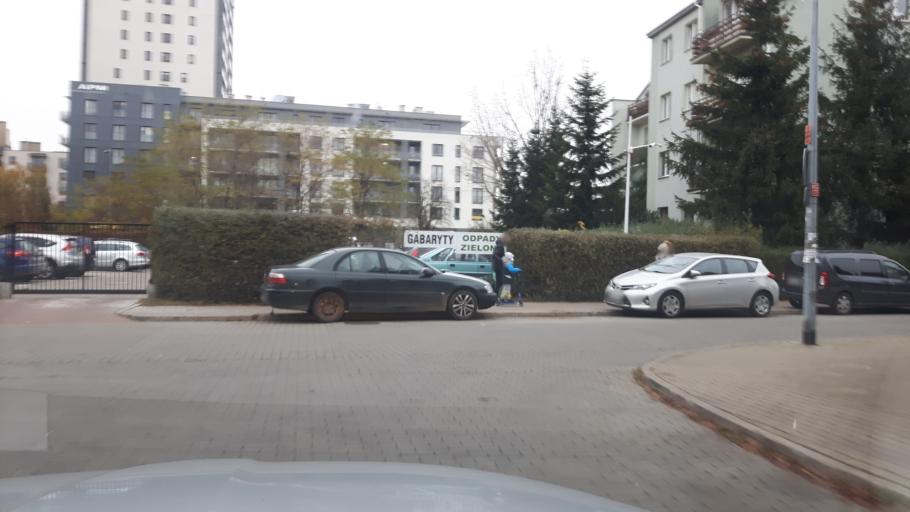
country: PL
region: Masovian Voivodeship
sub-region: Warszawa
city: Targowek
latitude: 52.2916
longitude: 21.0544
